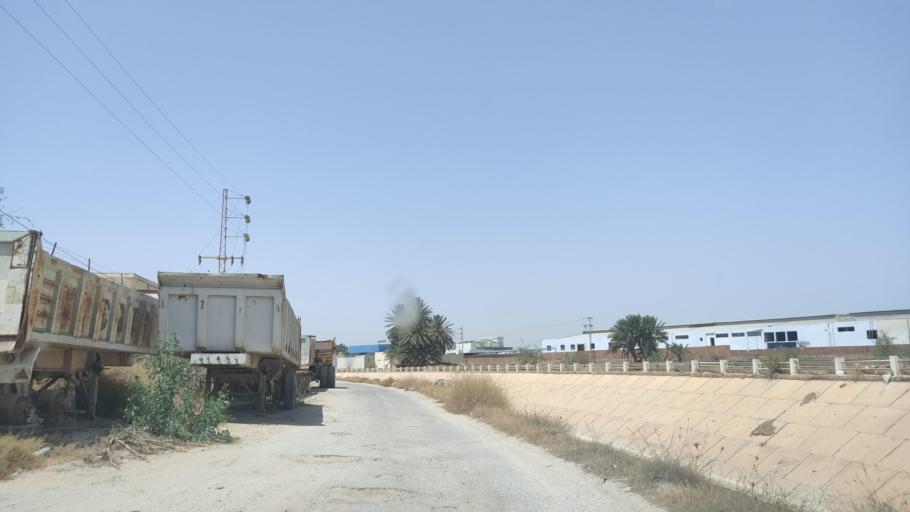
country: TN
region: Safaqis
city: Sfax
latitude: 34.7129
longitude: 10.7322
